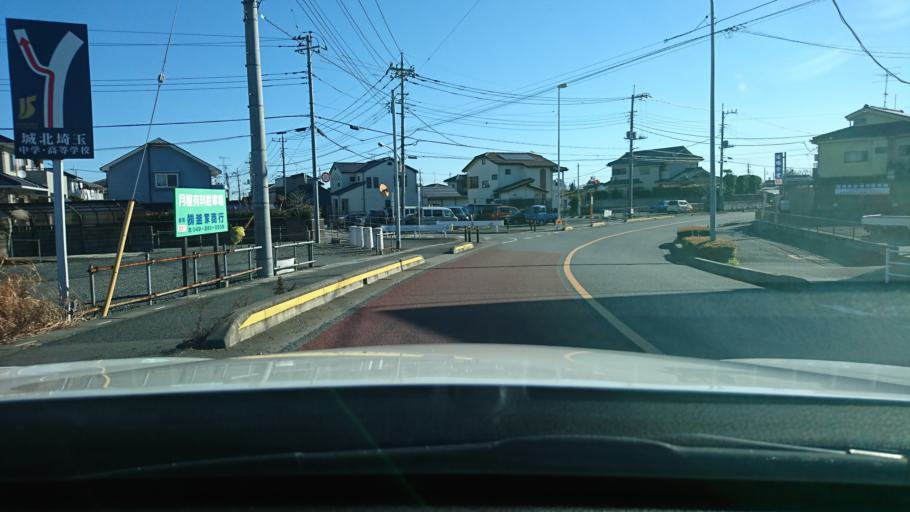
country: JP
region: Saitama
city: Kamifukuoka
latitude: 35.8859
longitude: 139.5243
